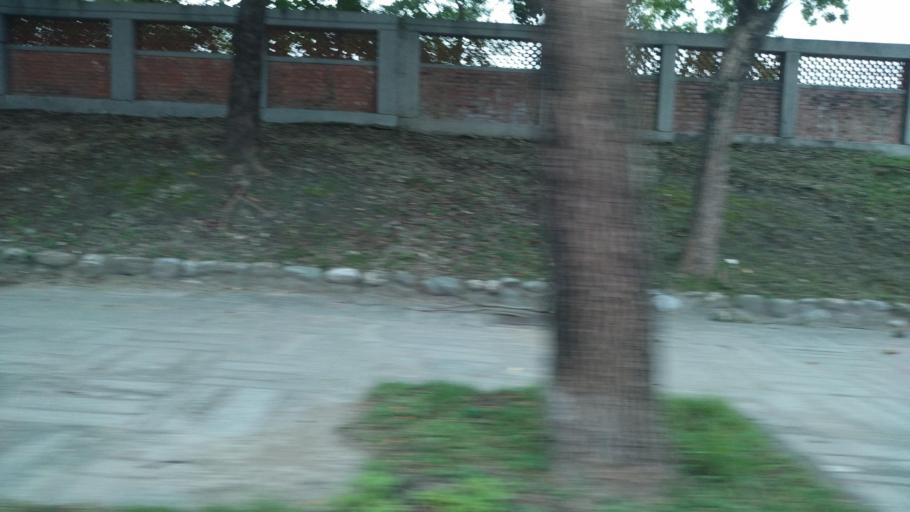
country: TW
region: Taiwan
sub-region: Hualien
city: Hualian
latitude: 24.0020
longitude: 121.6197
